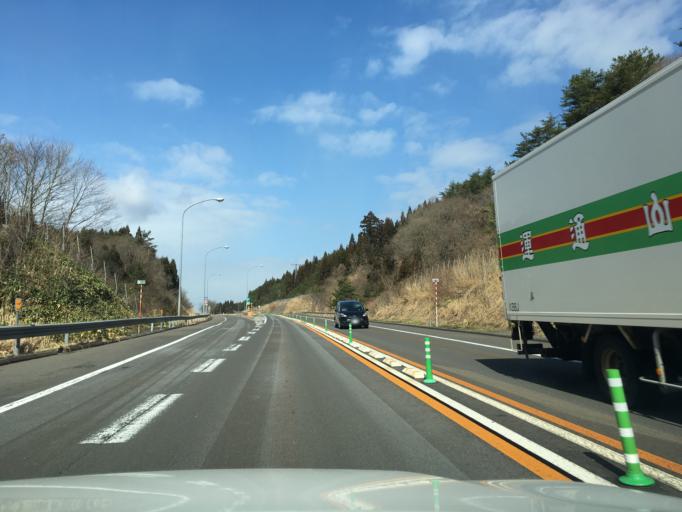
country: JP
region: Akita
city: Akita
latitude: 39.7469
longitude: 140.1566
